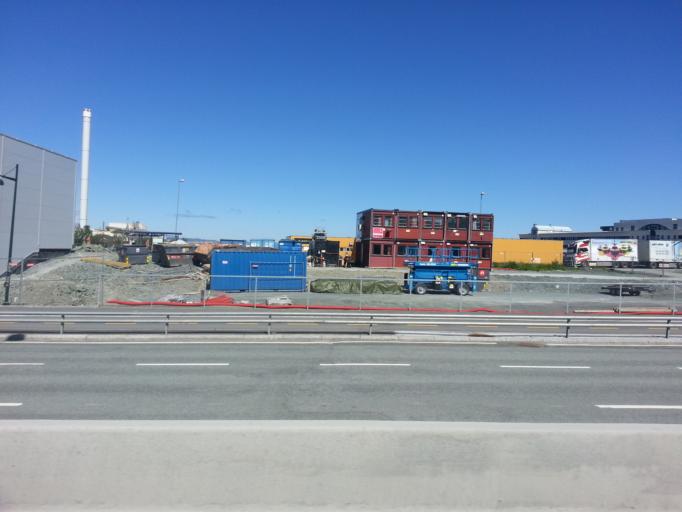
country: NO
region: Sor-Trondelag
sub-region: Trondheim
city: Trondheim
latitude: 63.4328
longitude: 10.4673
